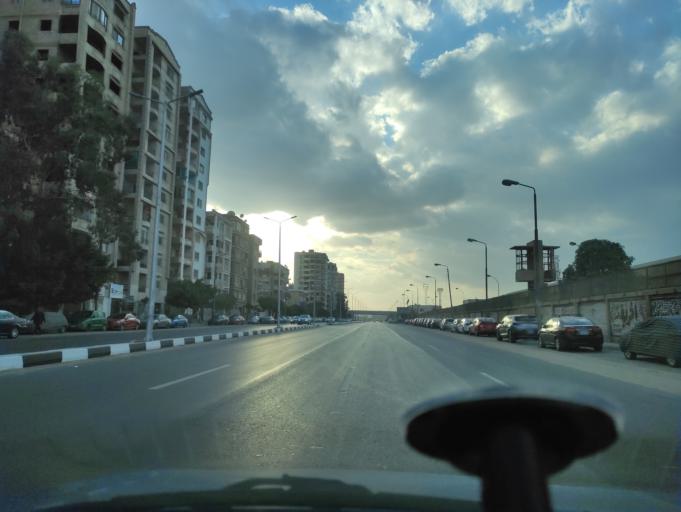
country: EG
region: Muhafazat al Qalyubiyah
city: Al Khankah
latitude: 30.1272
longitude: 31.3682
